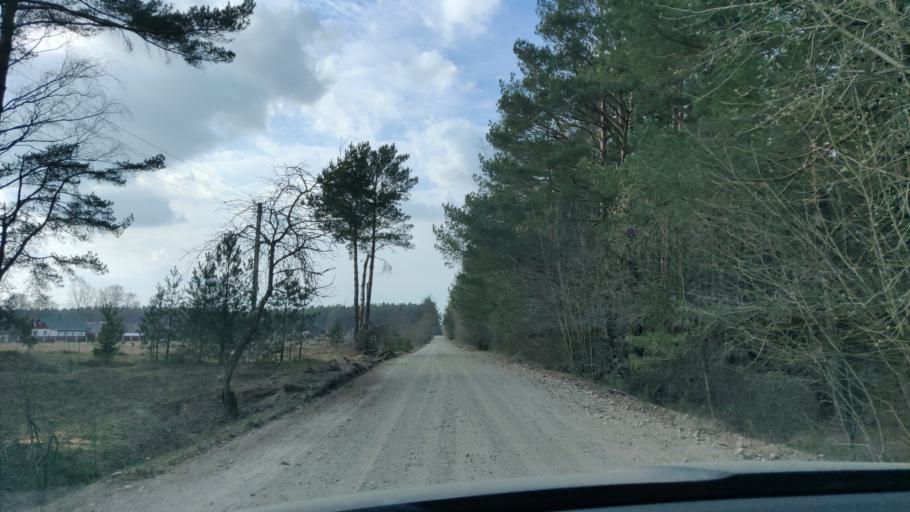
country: LT
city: Lentvaris
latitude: 54.5937
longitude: 25.0867
